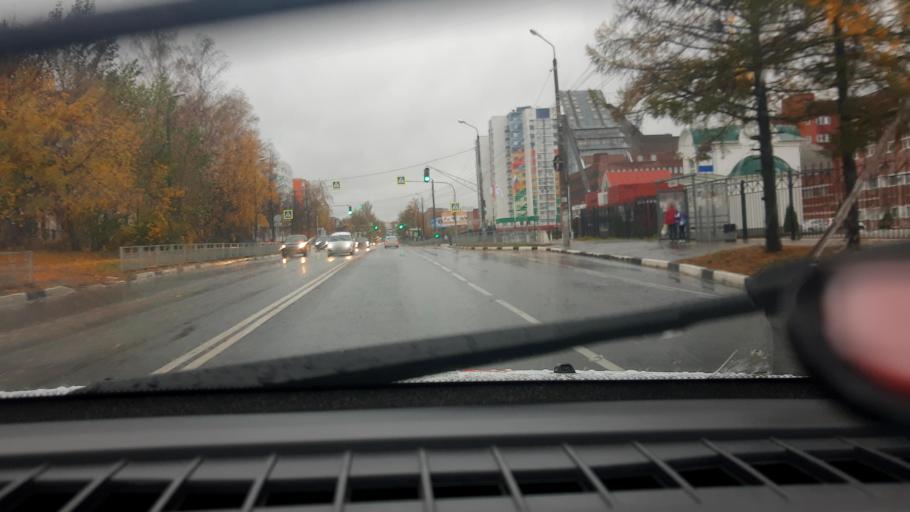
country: RU
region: Nizjnij Novgorod
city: Kstovo
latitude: 56.1529
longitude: 44.1905
